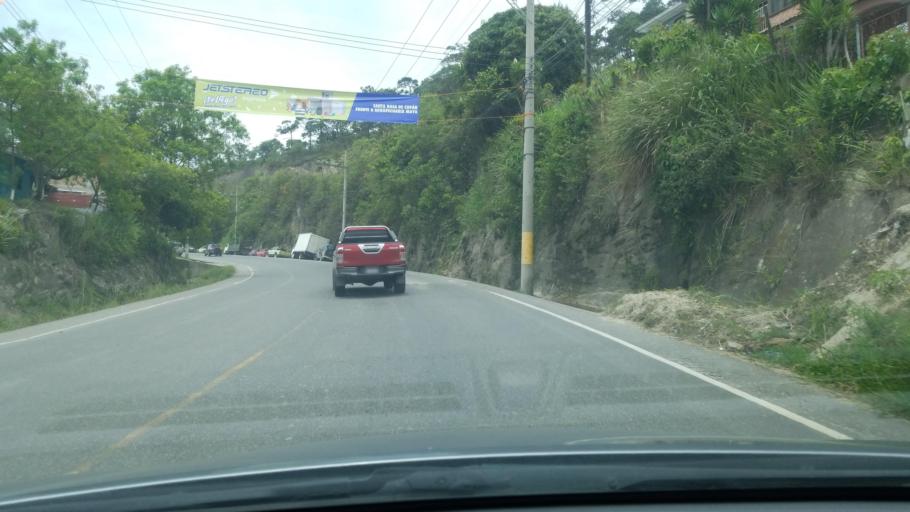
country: HN
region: Copan
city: Santa Rosa de Copan
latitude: 14.7581
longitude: -88.7768
